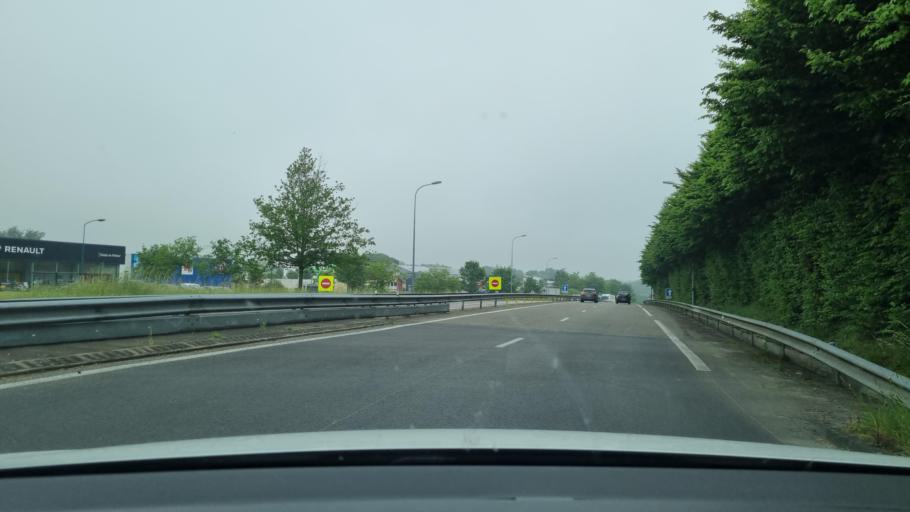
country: FR
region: Aquitaine
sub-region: Departement des Landes
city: Saint-Sever
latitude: 43.7473
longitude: -0.5613
